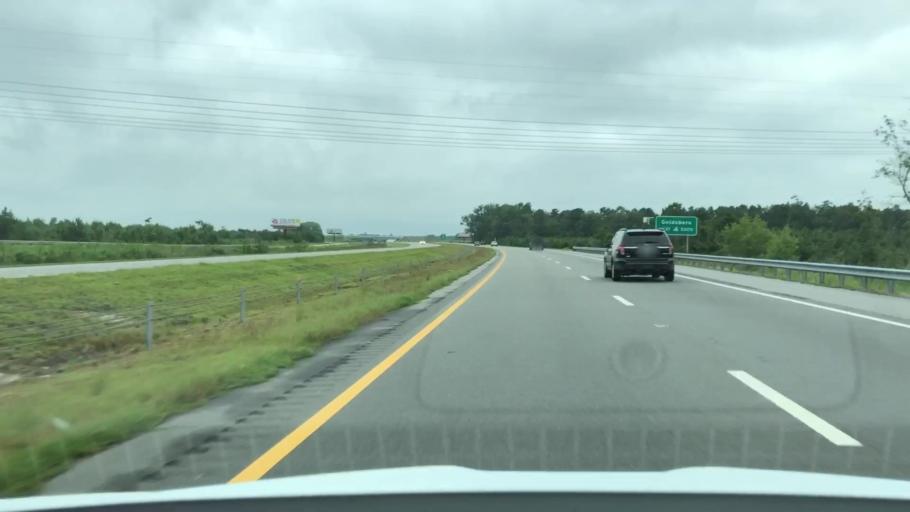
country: US
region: North Carolina
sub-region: Wayne County
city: Elroy
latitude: 35.3987
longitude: -77.8712
